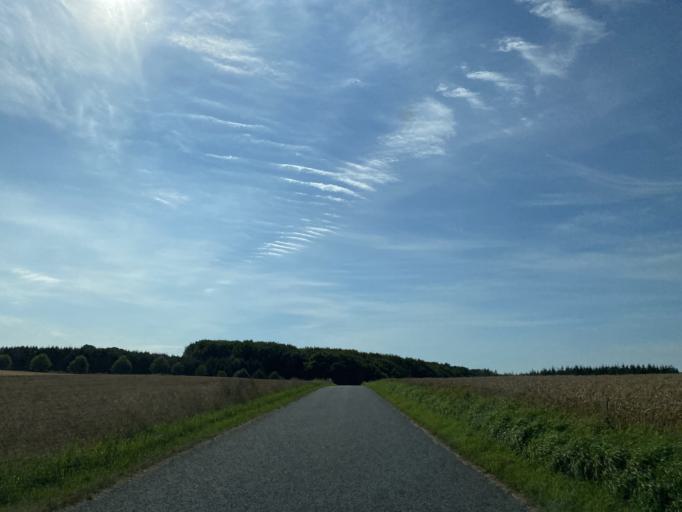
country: DK
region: Central Jutland
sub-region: Viborg Kommune
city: Bjerringbro
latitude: 56.3440
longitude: 9.7239
